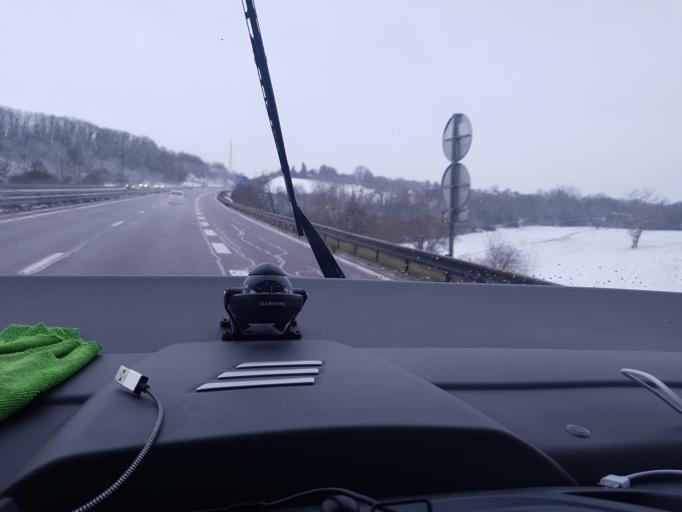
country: FR
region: Lorraine
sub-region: Departement de la Moselle
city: Saint-Julien-les-Metz
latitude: 49.1561
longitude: 6.2531
